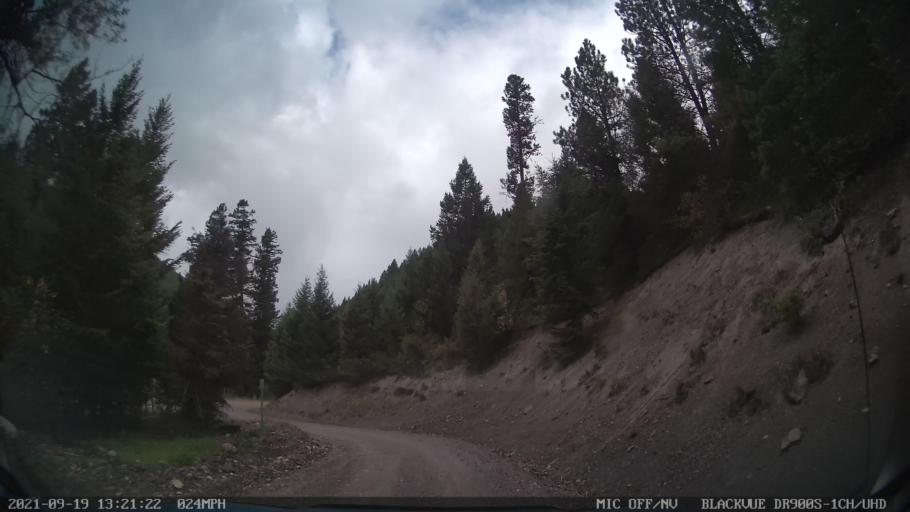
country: US
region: Montana
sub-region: Missoula County
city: Seeley Lake
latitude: 47.1678
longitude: -113.3530
